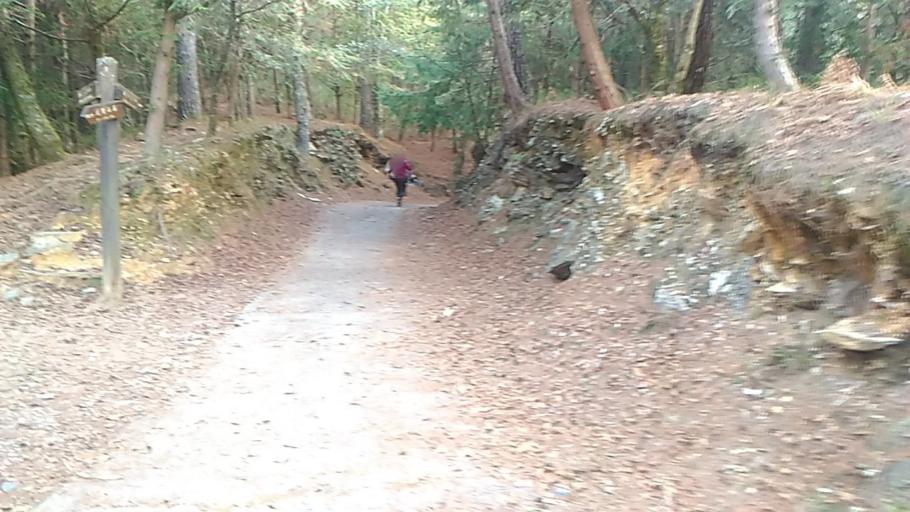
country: TW
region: Taiwan
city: Daxi
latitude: 24.4081
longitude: 121.3047
